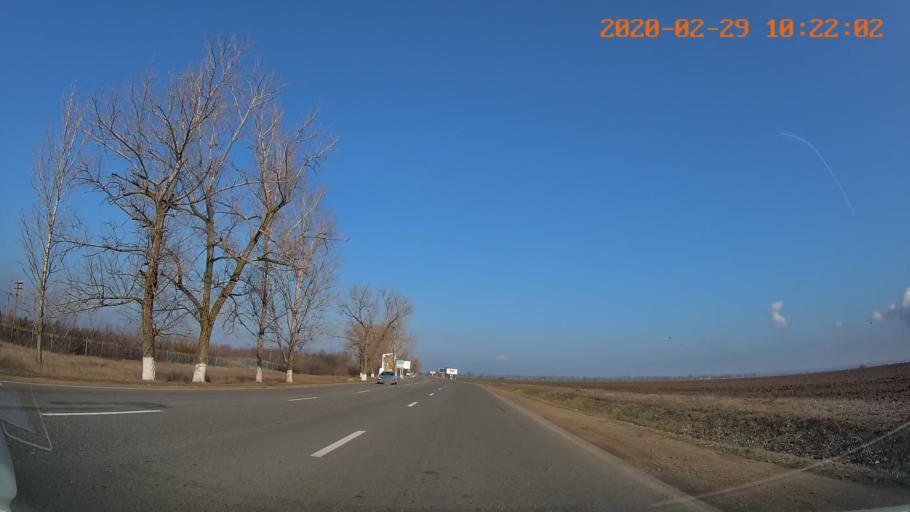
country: MD
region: Telenesti
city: Tiraspolul Nou
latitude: 46.8717
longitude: 29.6081
